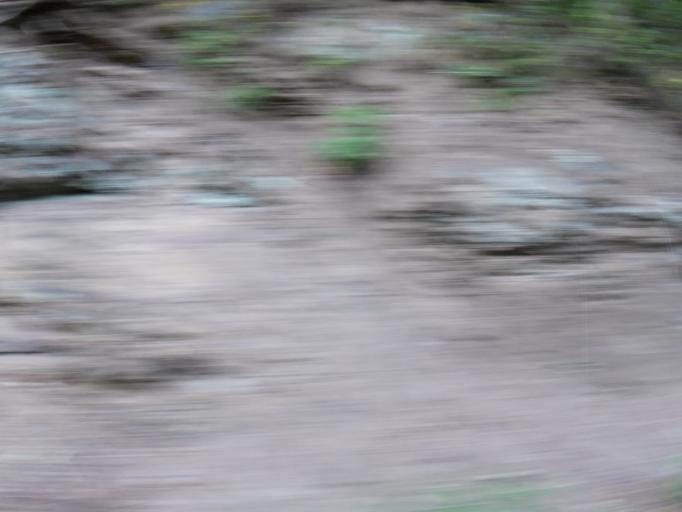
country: US
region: Tennessee
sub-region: Union County
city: Condon
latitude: 36.2113
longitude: -83.8288
